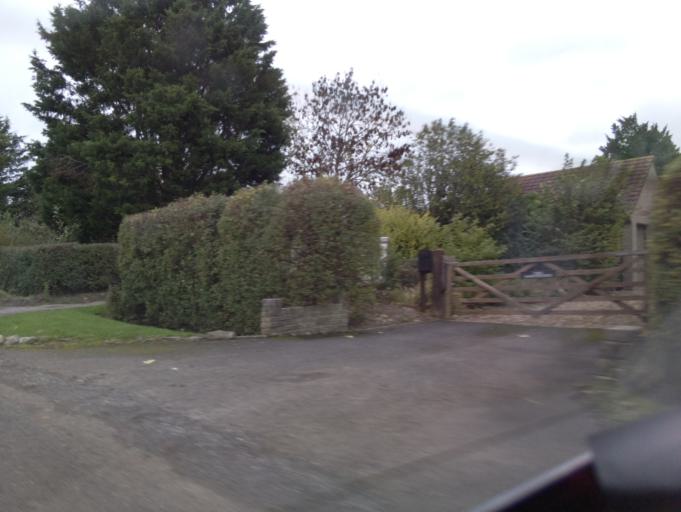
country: GB
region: England
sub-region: Somerset
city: Yeovil
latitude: 51.0100
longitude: -2.5980
